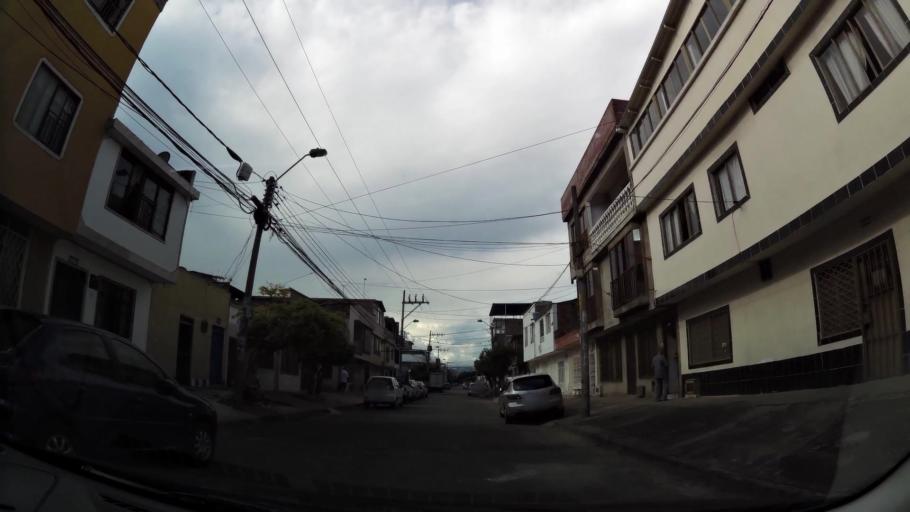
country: CO
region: Valle del Cauca
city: Cali
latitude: 3.4200
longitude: -76.5266
